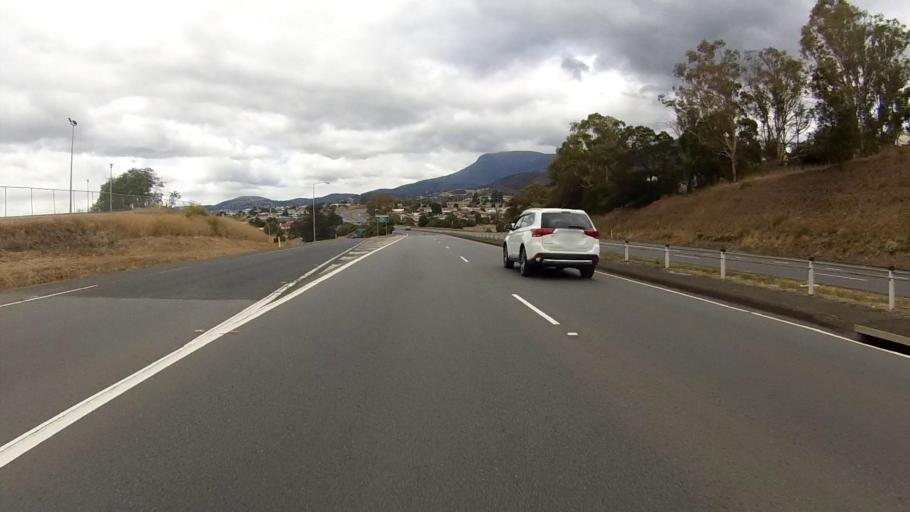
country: AU
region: Tasmania
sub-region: Glenorchy
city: Claremont
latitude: -42.7969
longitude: 147.2484
